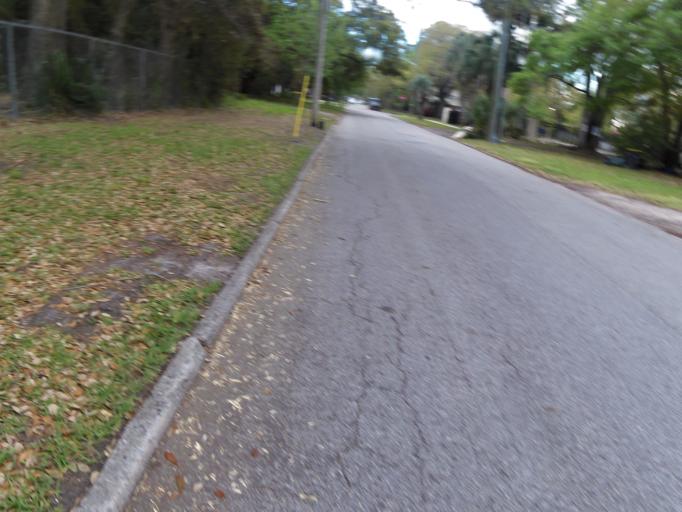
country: US
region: Florida
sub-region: Duval County
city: Jacksonville
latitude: 30.3112
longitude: -81.6593
